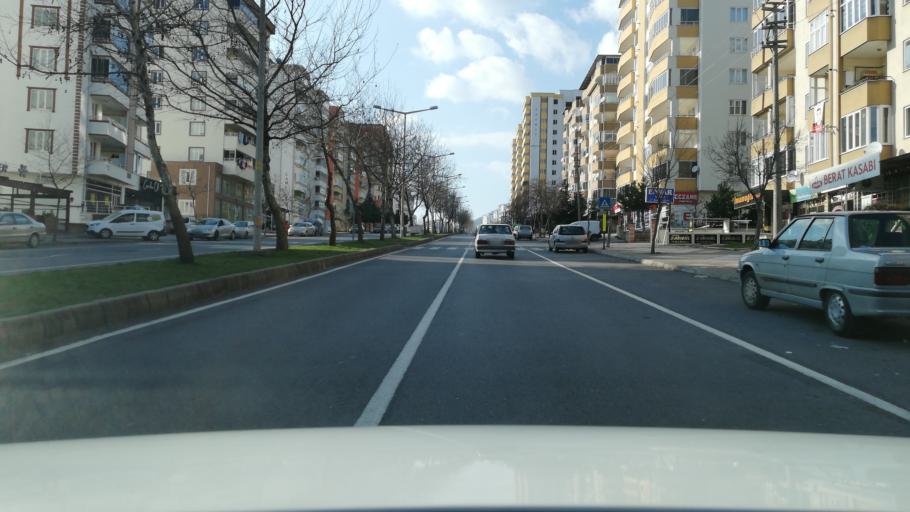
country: TR
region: Kahramanmaras
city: Kahramanmaras
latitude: 37.5934
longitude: 36.8966
